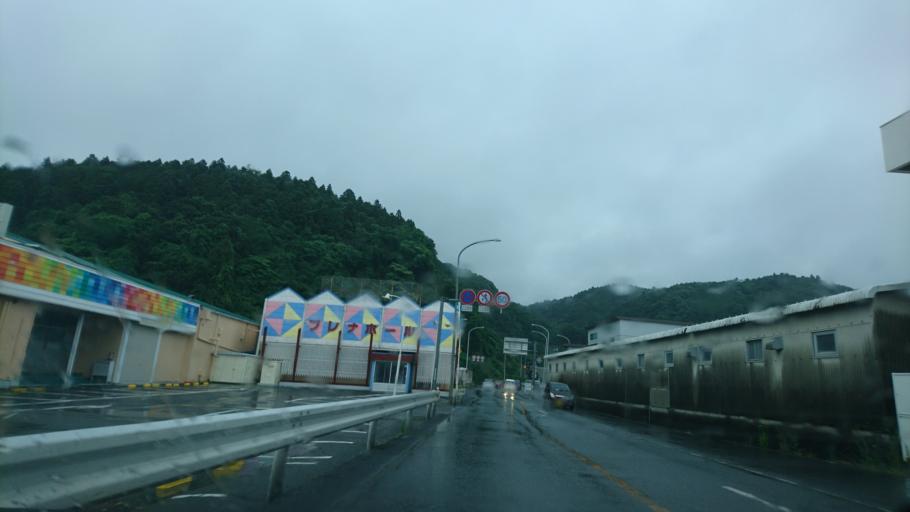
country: JP
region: Miyagi
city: Ishinomaki
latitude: 38.4364
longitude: 141.3187
